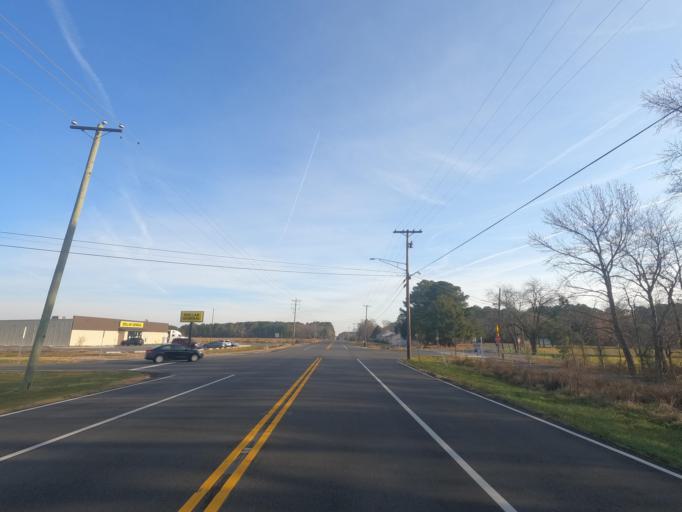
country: US
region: Maryland
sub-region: Somerset County
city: Crisfield
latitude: 38.0330
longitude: -75.7811
